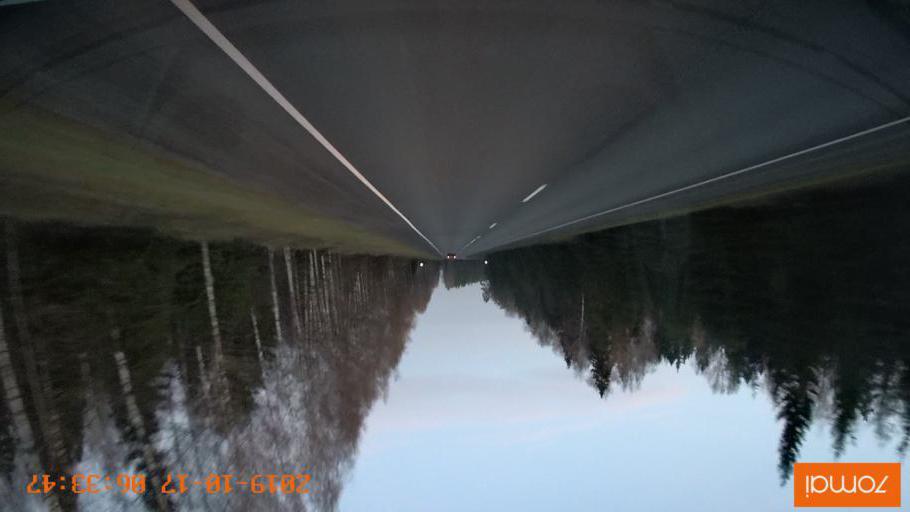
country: RU
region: Ivanovo
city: Novoye Leushino
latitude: 56.7099
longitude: 40.6510
